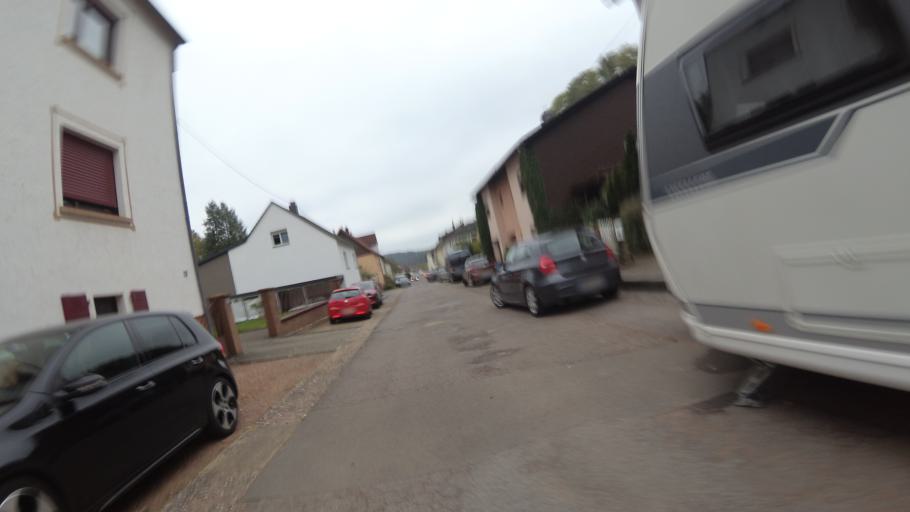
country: DE
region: Saarland
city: Blieskastel
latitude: 49.2697
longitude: 7.2908
